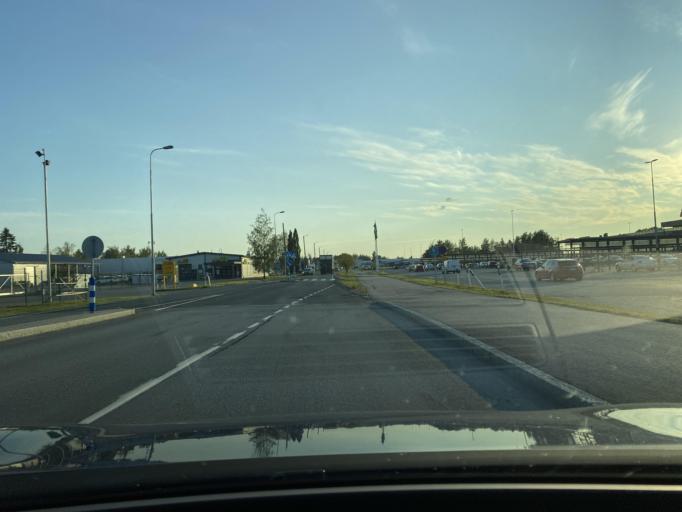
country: FI
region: Southern Ostrobothnia
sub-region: Seinaejoki
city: Nurmo
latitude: 62.8052
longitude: 22.8789
